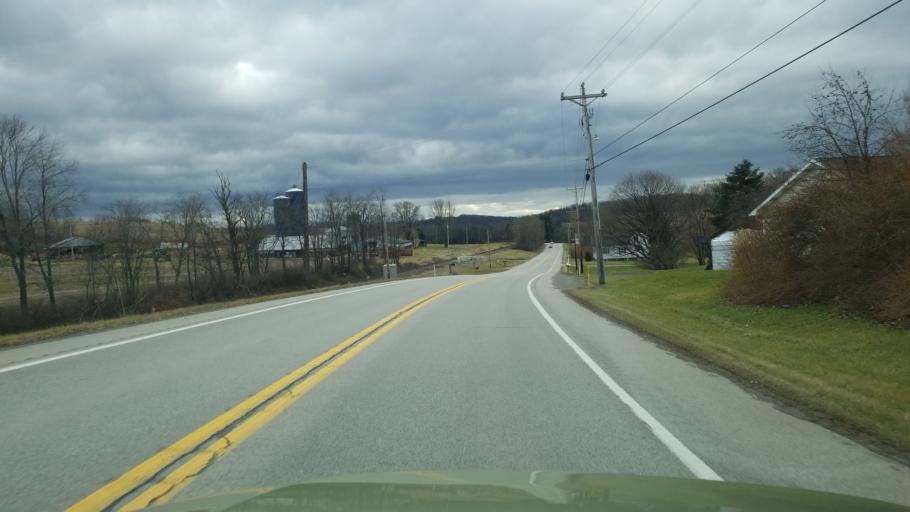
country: US
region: Pennsylvania
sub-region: Indiana County
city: Clymer
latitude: 40.7943
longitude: -79.0538
